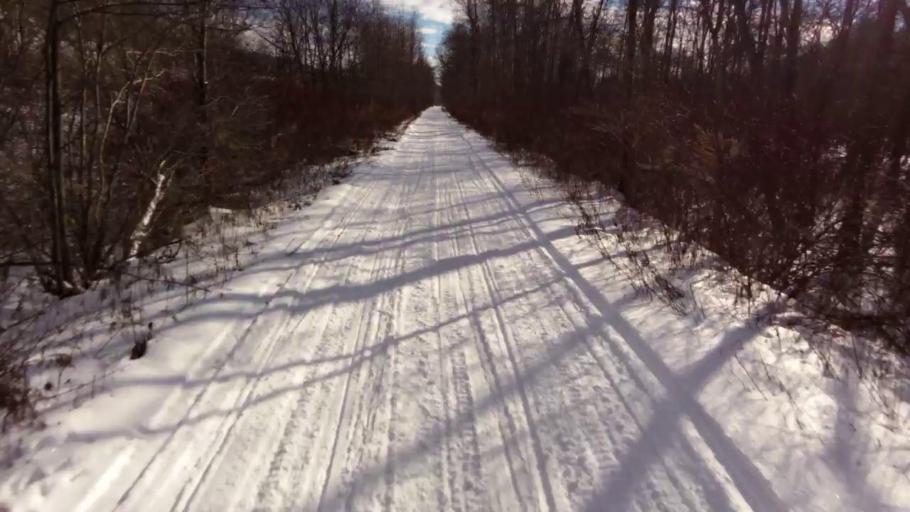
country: US
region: Pennsylvania
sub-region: McKean County
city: Foster Brook
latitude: 42.0134
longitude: -78.6264
